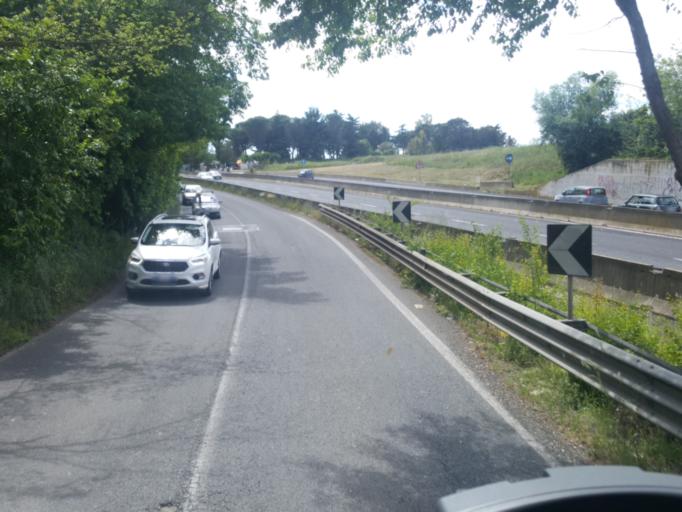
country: IT
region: Latium
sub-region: Citta metropolitana di Roma Capitale
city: La Massimina-Casal Lumbroso
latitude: 41.8863
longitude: 12.3641
